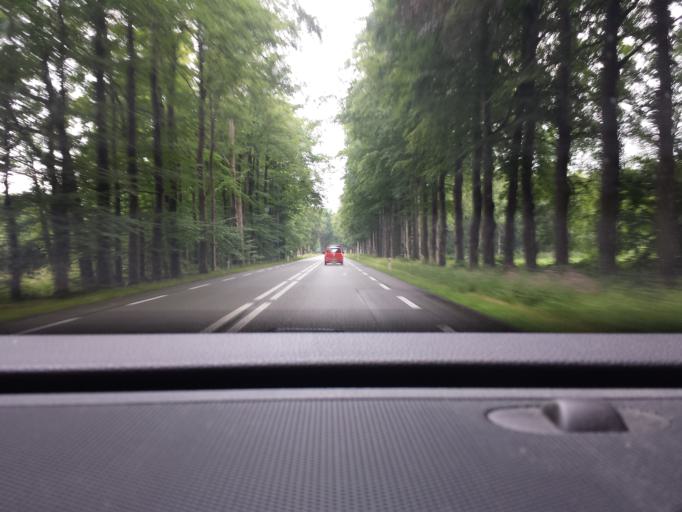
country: NL
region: Gelderland
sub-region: Gemeente Lochem
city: Lochem
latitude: 52.0989
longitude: 6.3753
